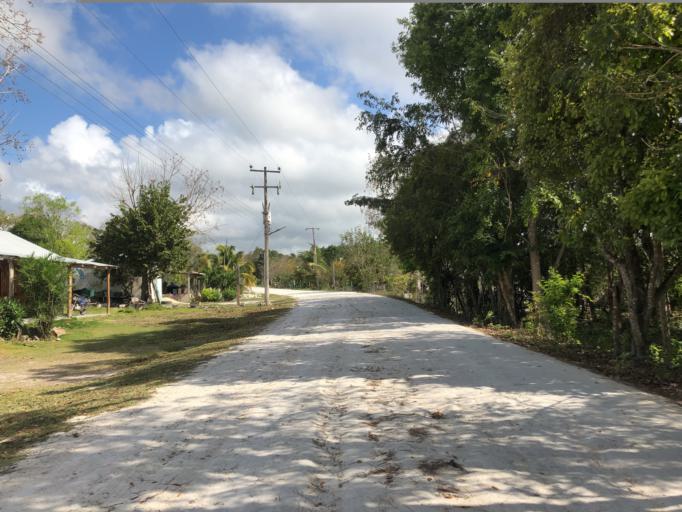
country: MX
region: Quintana Roo
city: Nicolas Bravo
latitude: 18.4545
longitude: -89.3058
